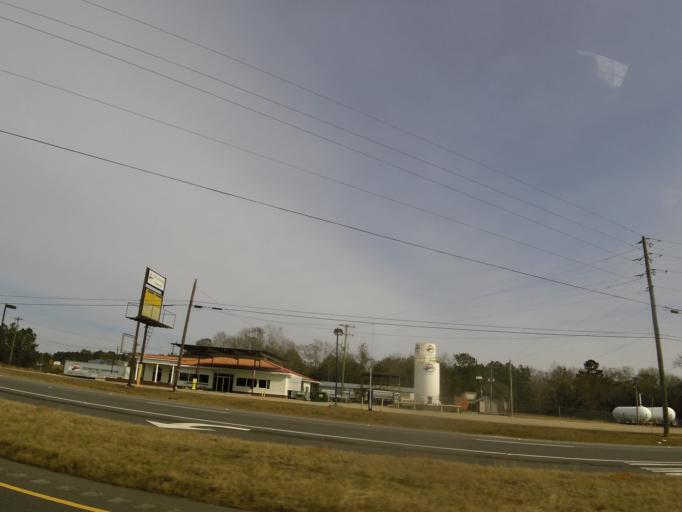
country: US
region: Alabama
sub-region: Dale County
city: Ozark
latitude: 31.4941
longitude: -85.6916
